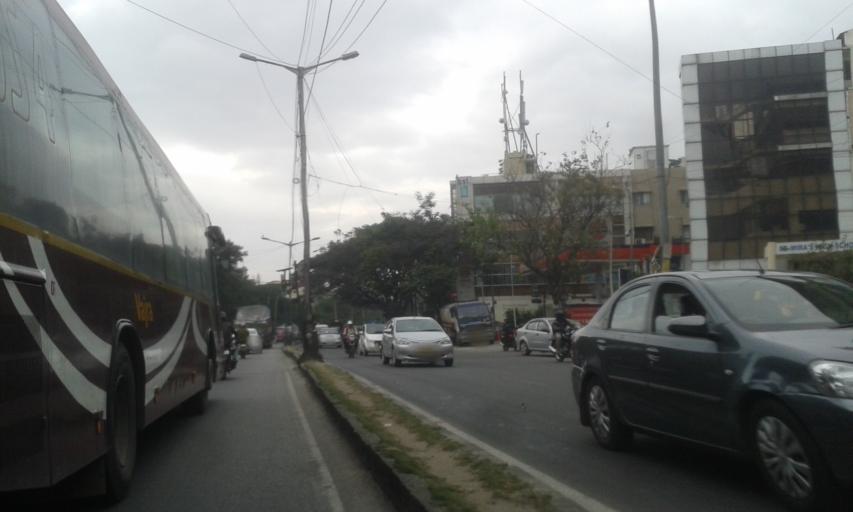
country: IN
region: Karnataka
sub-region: Bangalore Urban
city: Bangalore
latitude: 12.9166
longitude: 77.6205
